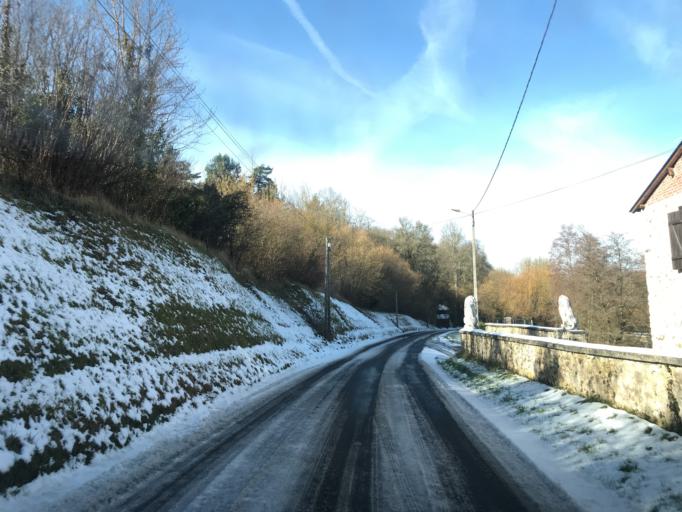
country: FR
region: Haute-Normandie
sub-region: Departement de l'Eure
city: Saint-Aubin-sur-Gaillon
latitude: 49.0830
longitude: 1.2750
